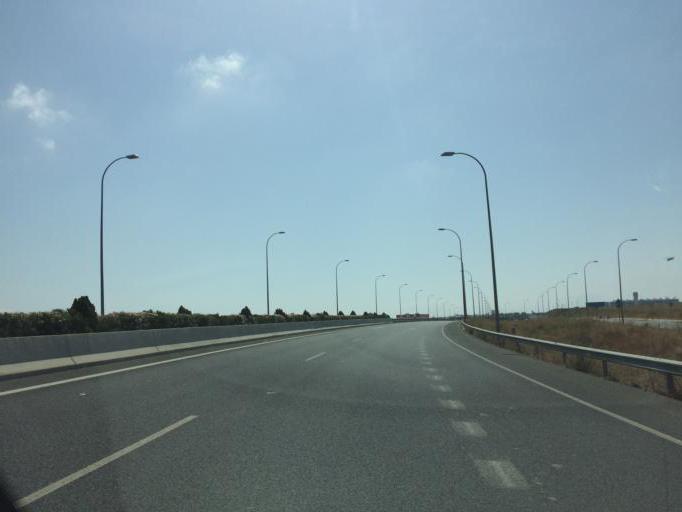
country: ES
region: Andalusia
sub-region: Provincia de Malaga
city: Alhaurin de la Torre
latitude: 36.6889
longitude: -4.5107
